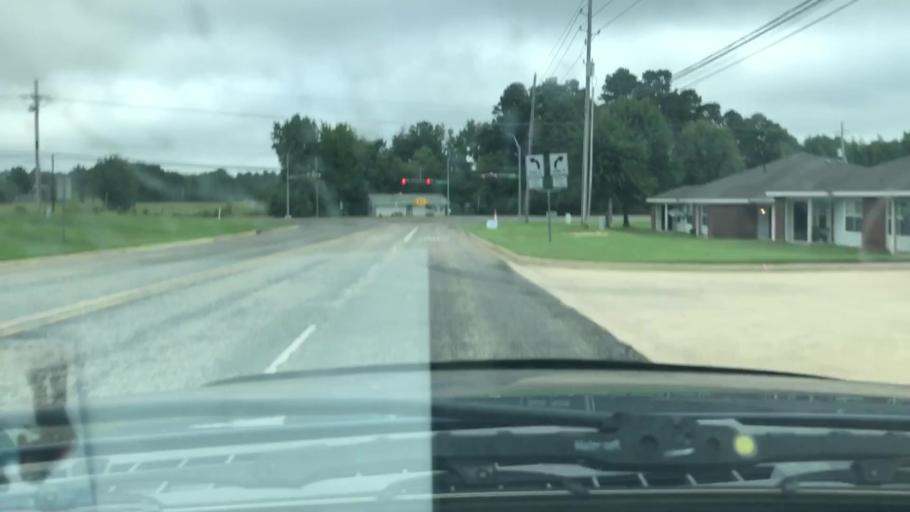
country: US
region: Texas
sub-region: Bowie County
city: Wake Village
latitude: 33.3957
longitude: -94.0920
